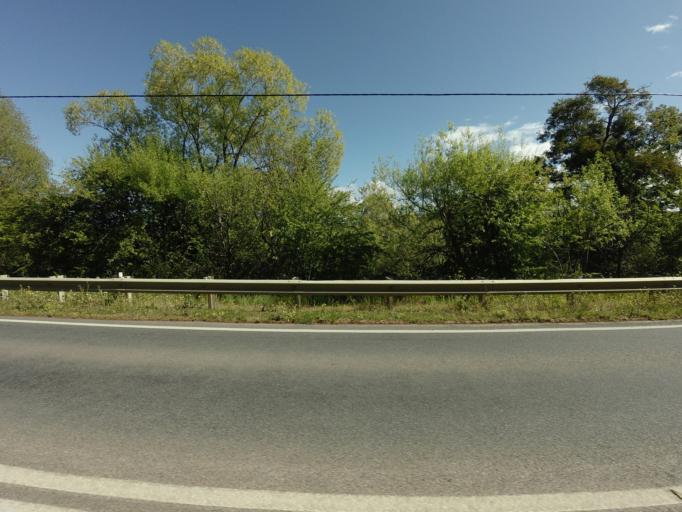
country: AU
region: Tasmania
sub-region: Derwent Valley
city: New Norfolk
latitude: -42.7406
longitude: 146.9826
